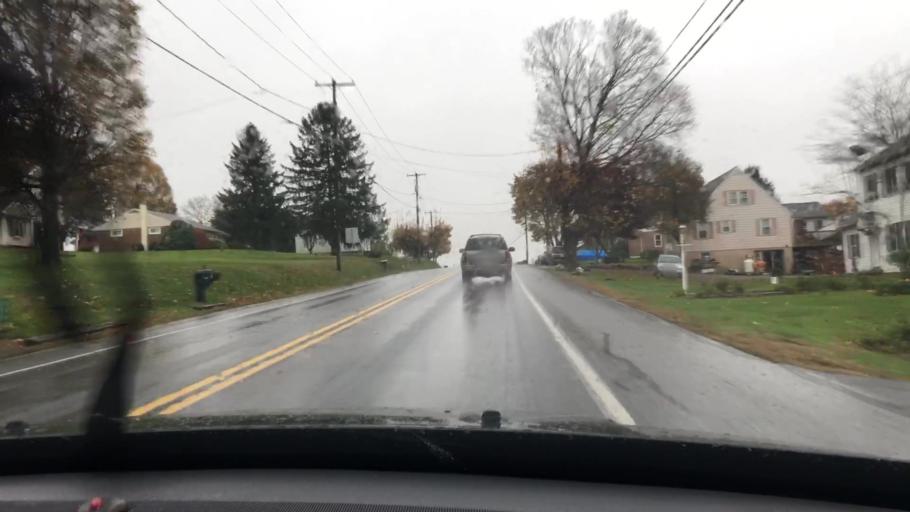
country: US
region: Pennsylvania
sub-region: Lancaster County
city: Quarryville
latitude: 39.8951
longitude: -76.2403
